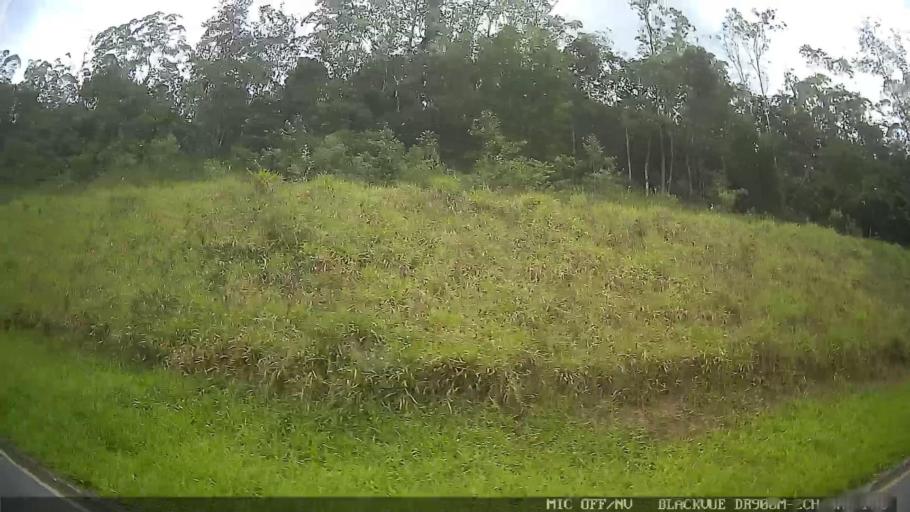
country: BR
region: Sao Paulo
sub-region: Ribeirao Pires
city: Ribeirao Pires
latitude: -23.7236
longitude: -46.4074
